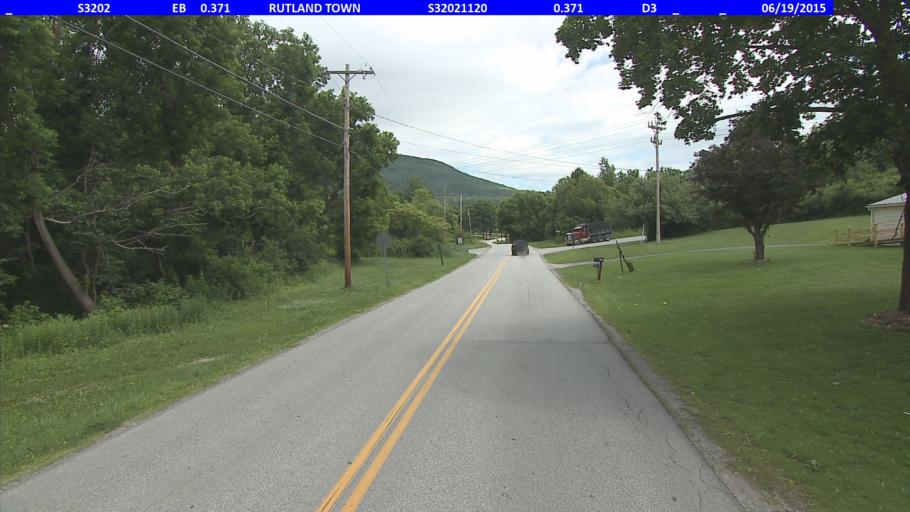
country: US
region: Vermont
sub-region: Rutland County
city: Rutland
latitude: 43.5889
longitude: -72.9617
